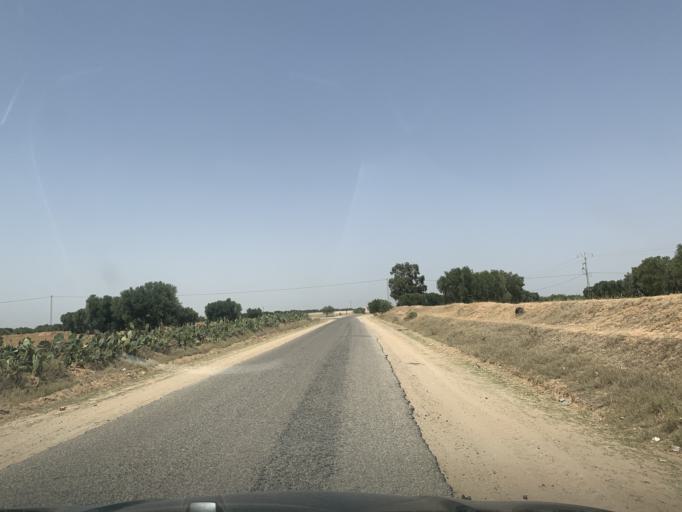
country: TN
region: Al Mahdiyah
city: Shurban
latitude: 35.1797
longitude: 10.2358
